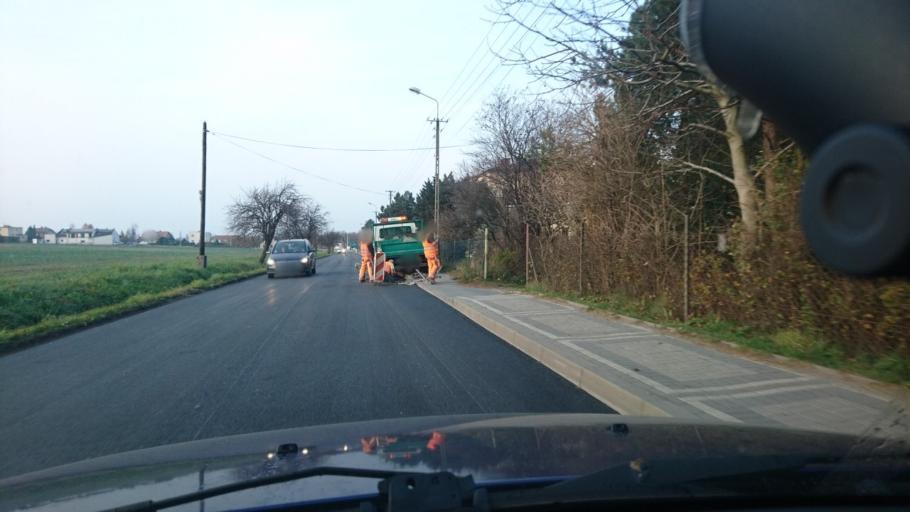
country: PL
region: Silesian Voivodeship
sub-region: Powiat bielski
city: Jaworze
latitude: 49.8028
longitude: 18.9424
